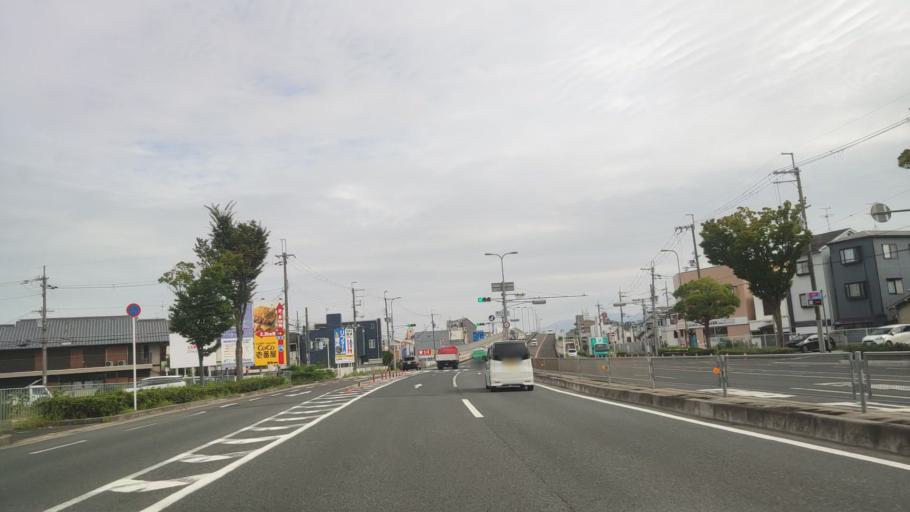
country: JP
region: Osaka
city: Kashihara
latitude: 34.5563
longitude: 135.5985
